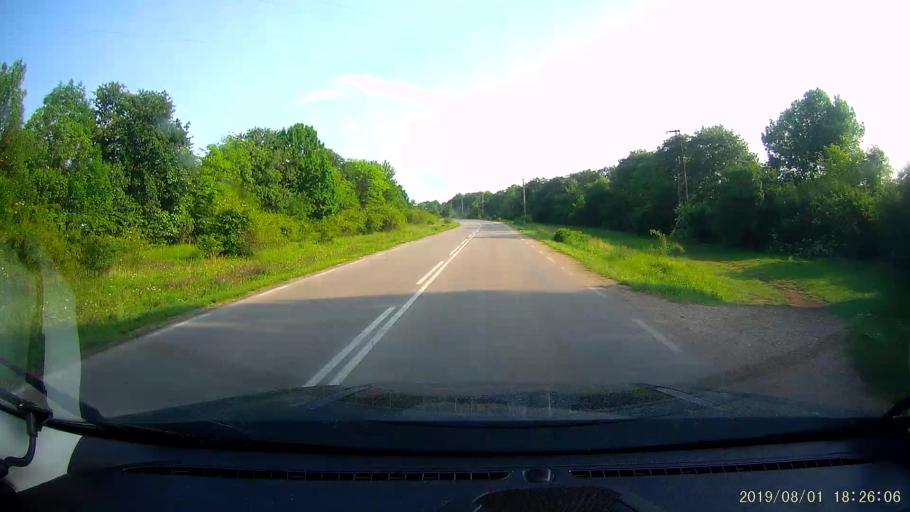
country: BG
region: Shumen
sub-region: Obshtina Venets
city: Venets
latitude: 43.6070
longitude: 26.9946
